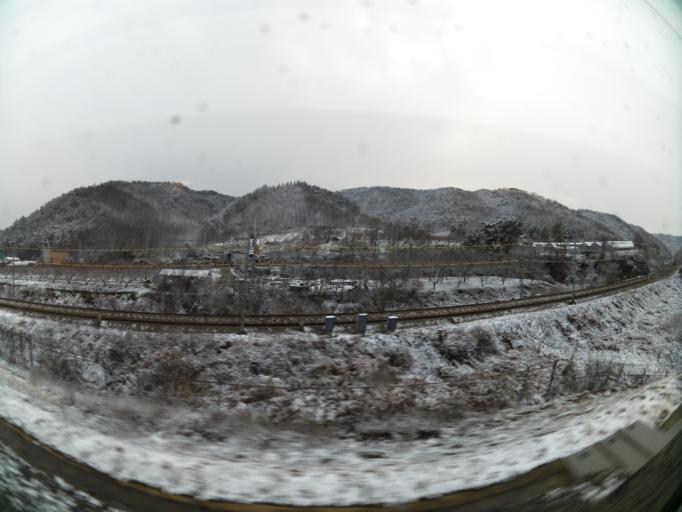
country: KR
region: Chungcheongbuk-do
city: Yong-dong
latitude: 36.1969
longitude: 127.7554
